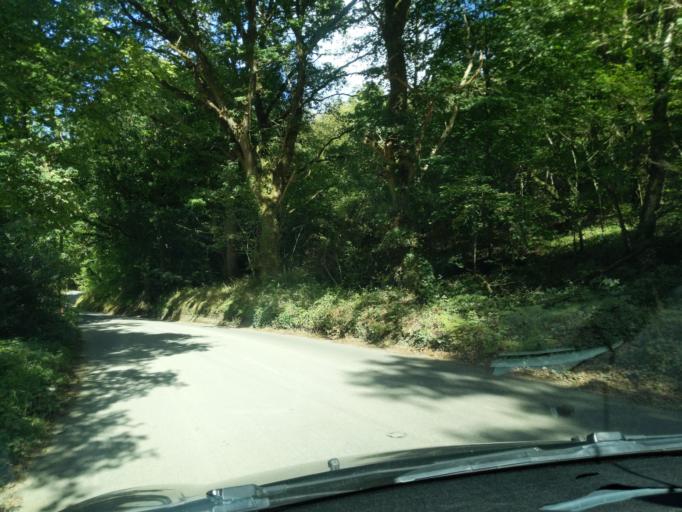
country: GB
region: England
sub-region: Devon
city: Great Torrington
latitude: 50.9375
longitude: -4.1805
